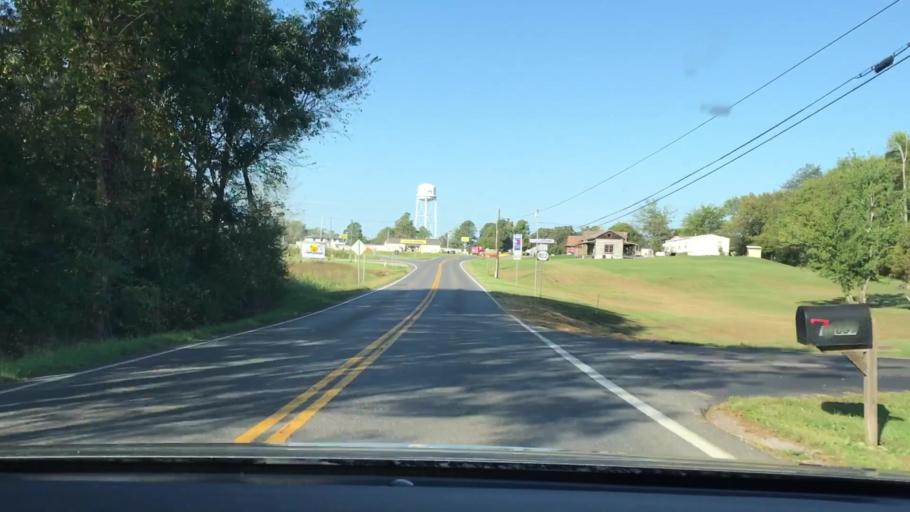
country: US
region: Kentucky
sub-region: Marshall County
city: Benton
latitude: 36.7767
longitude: -88.1555
